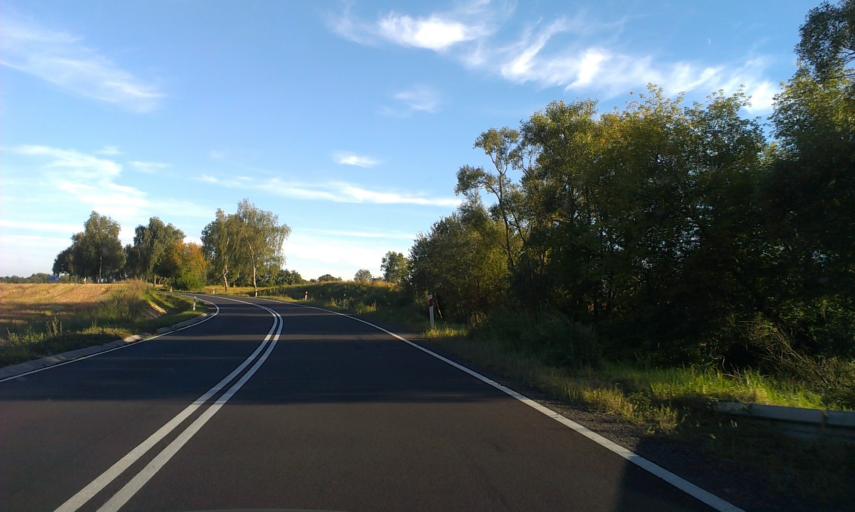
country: PL
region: West Pomeranian Voivodeship
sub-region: Powiat szczecinecki
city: Szczecinek
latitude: 53.7587
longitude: 16.6480
